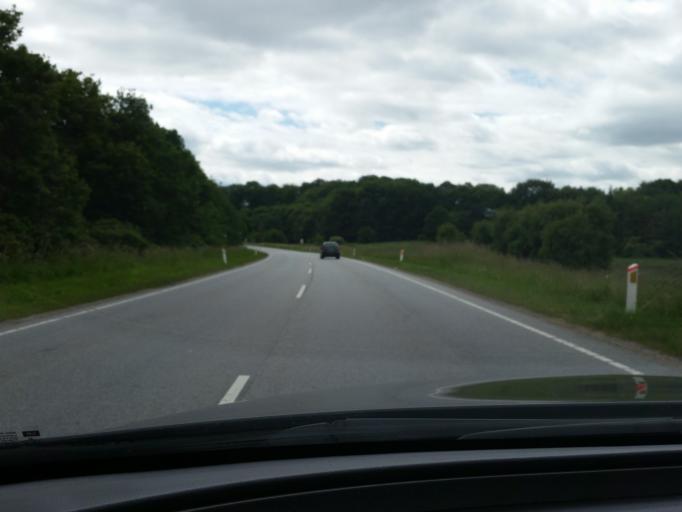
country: DK
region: Central Jutland
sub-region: Horsens Kommune
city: Horsens
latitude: 55.8813
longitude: 9.8244
